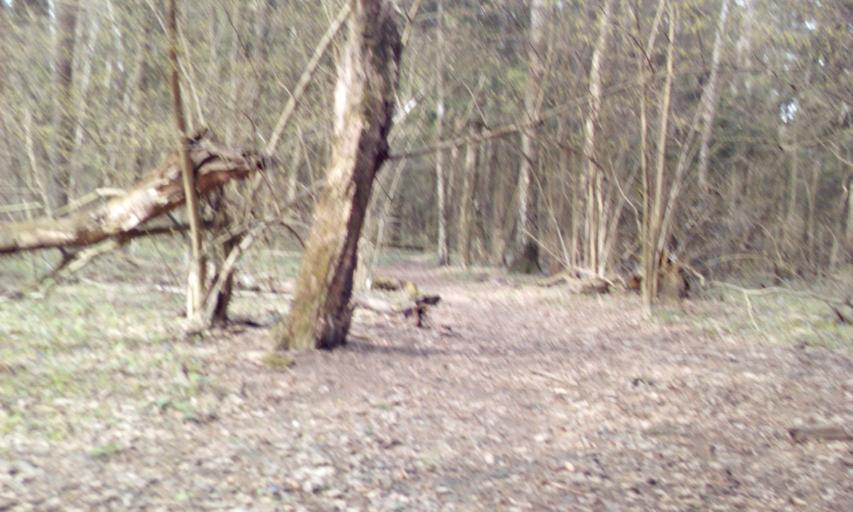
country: RU
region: Moskovskaya
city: Lesnoy Gorodok
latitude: 55.6392
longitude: 37.2525
